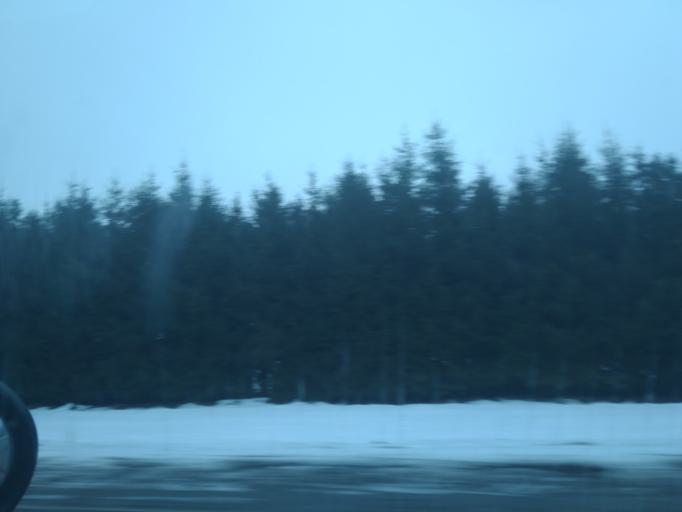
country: BY
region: Minsk
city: Haradzyeya
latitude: 53.3616
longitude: 26.5137
